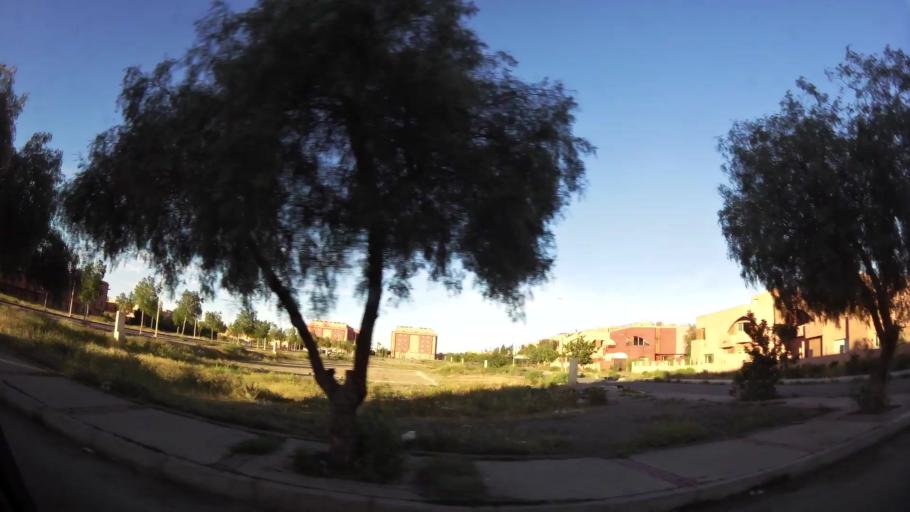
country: MA
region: Marrakech-Tensift-Al Haouz
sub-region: Marrakech
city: Marrakesh
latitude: 31.7469
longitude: -8.1093
